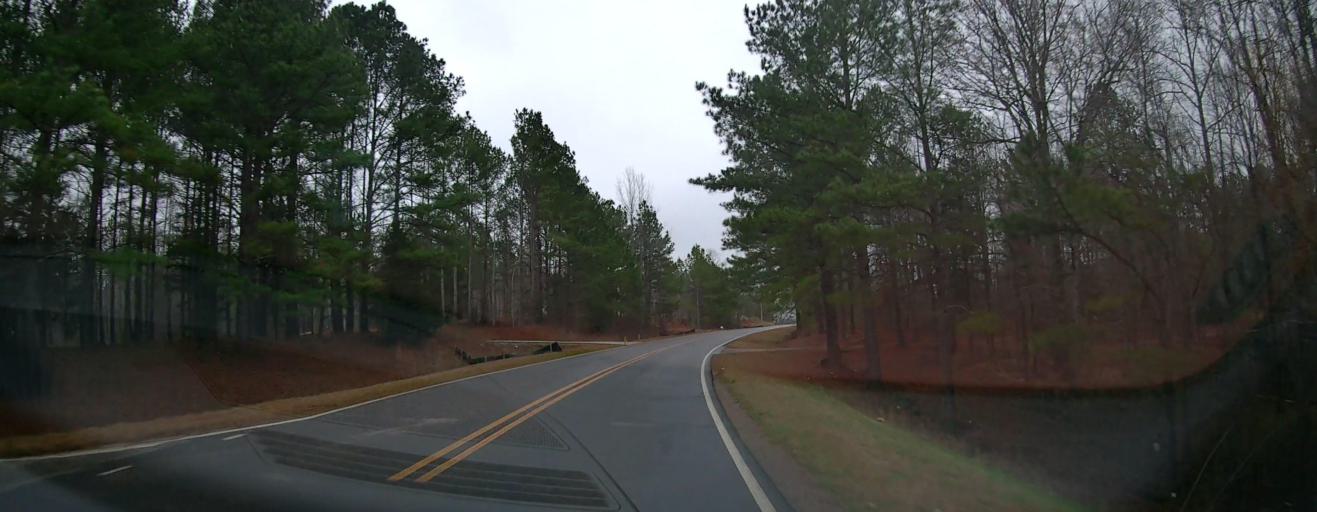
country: US
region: Georgia
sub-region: Pike County
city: Zebulon
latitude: 33.1265
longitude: -84.3464
